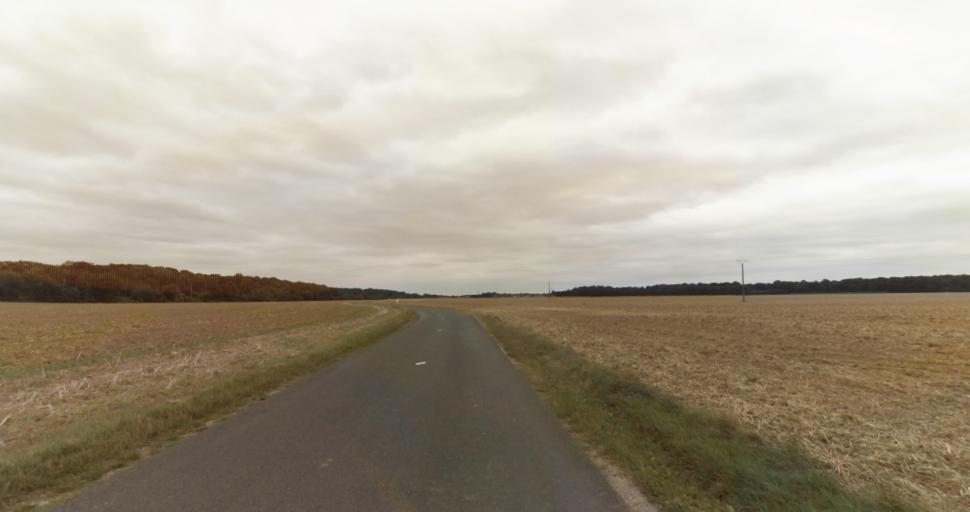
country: FR
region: Haute-Normandie
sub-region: Departement de l'Eure
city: Evreux
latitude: 49.0020
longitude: 1.2027
